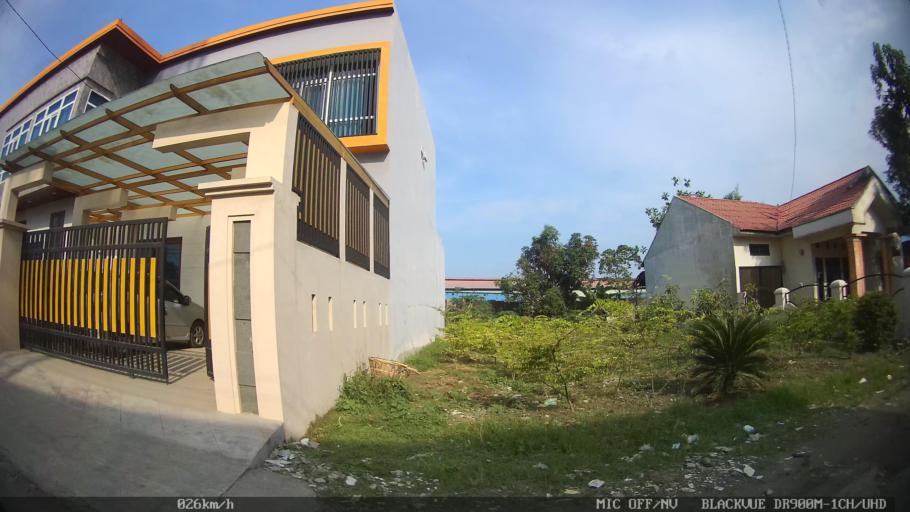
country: ID
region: North Sumatra
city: Medan
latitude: 3.6004
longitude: 98.7414
